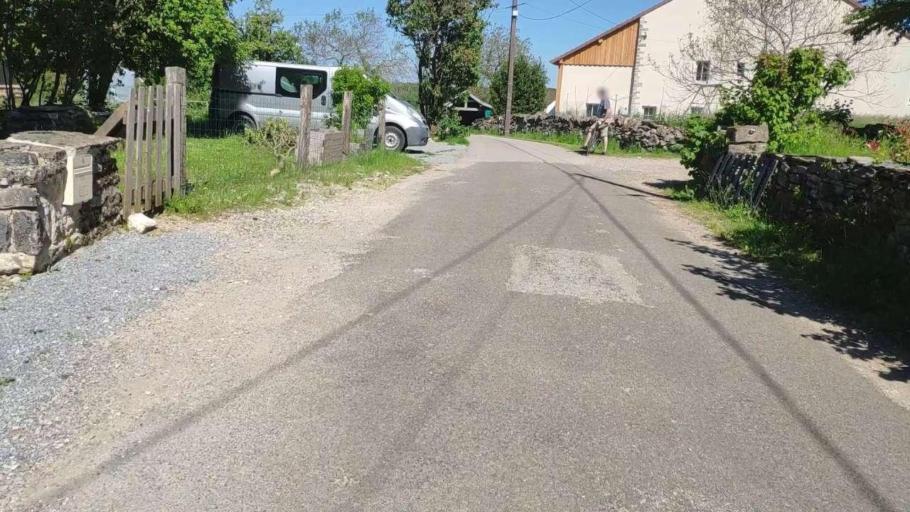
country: FR
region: Franche-Comte
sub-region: Departement du Jura
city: Clairvaux-les-Lacs
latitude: 46.6997
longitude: 5.7285
